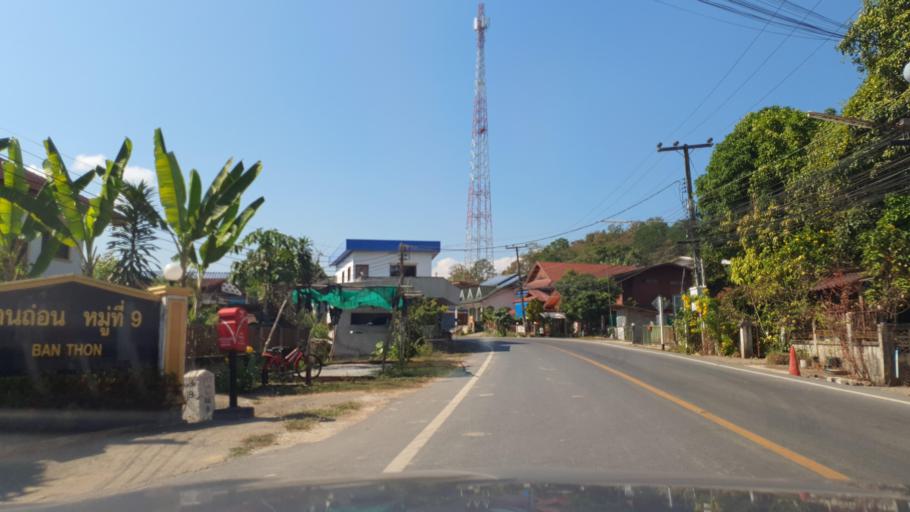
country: TH
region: Nan
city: Tha Wang Pha
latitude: 19.0822
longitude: 100.8795
